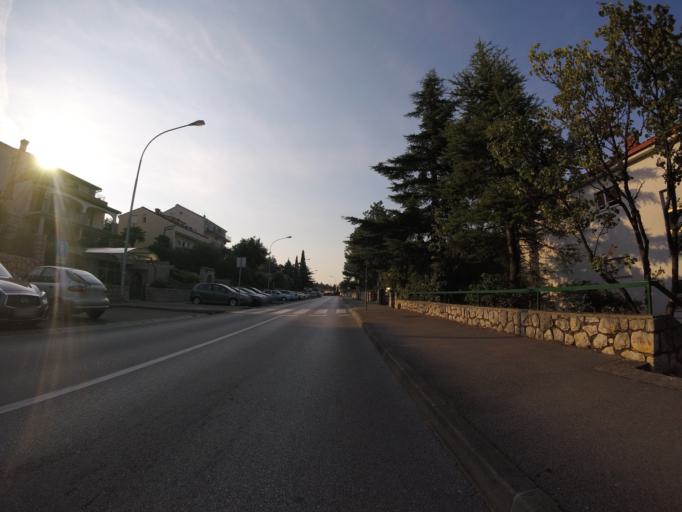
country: HR
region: Primorsko-Goranska
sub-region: Grad Crikvenica
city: Crikvenica
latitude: 45.1839
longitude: 14.6804
